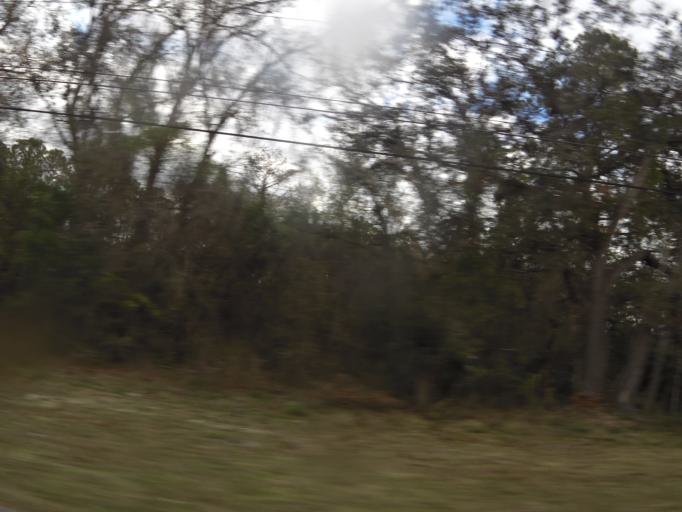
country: US
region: Florida
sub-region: Volusia County
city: Pierson
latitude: 29.2773
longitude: -81.4762
